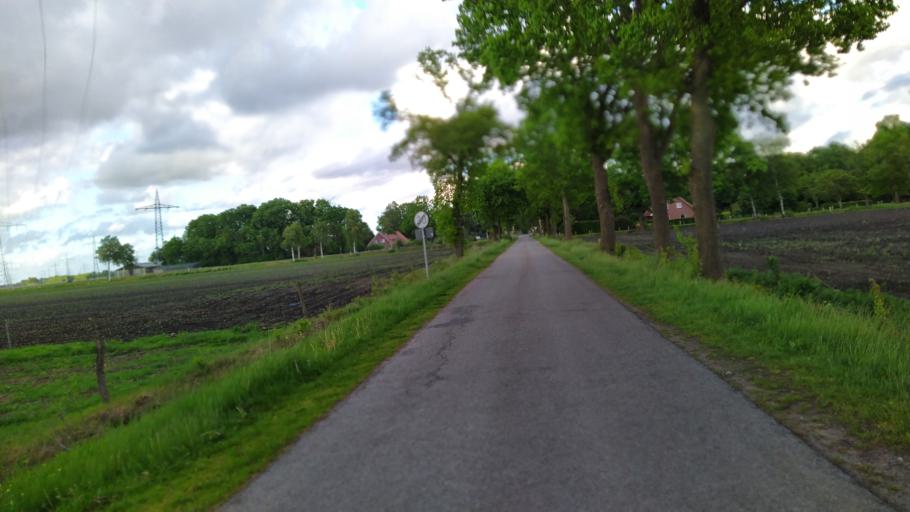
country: DE
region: Lower Saxony
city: Bargstedt
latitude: 53.4779
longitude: 9.4170
